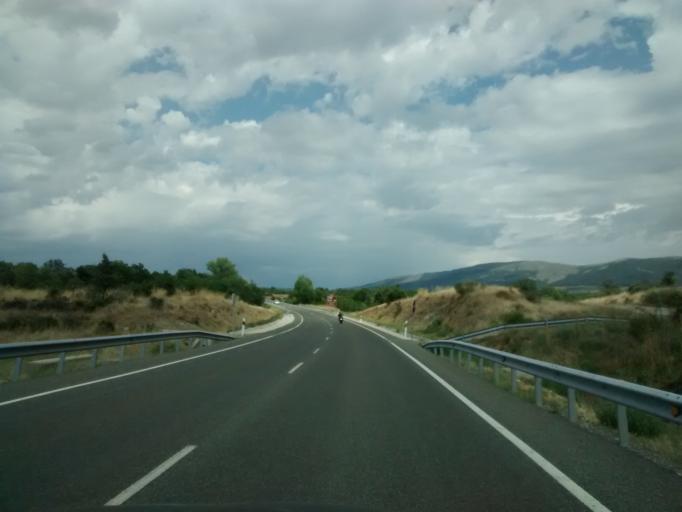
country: ES
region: Castille and Leon
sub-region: Provincia de Segovia
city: Navafria
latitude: 41.0642
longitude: -3.8258
